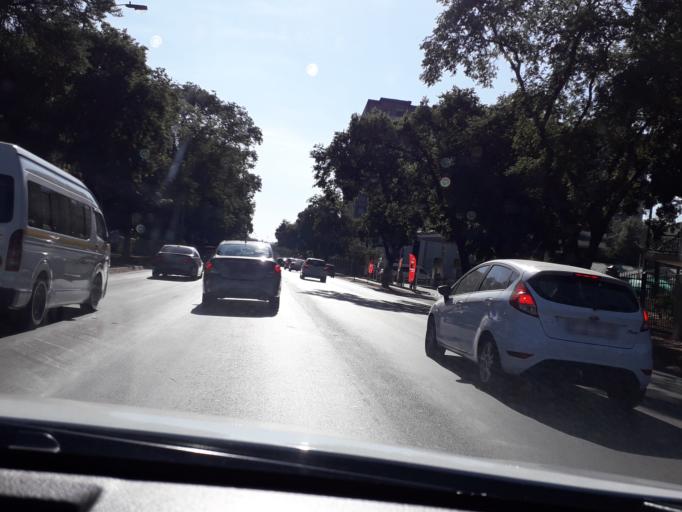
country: ZA
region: Gauteng
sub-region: City of Tshwane Metropolitan Municipality
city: Pretoria
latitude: -25.7462
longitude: 28.2349
